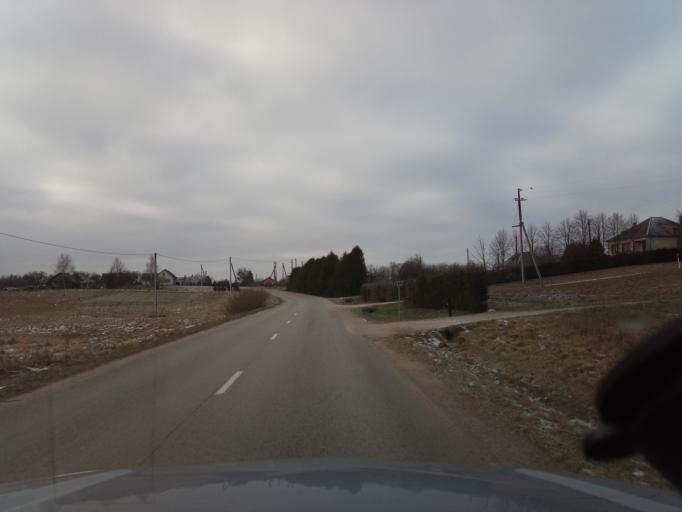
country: LT
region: Alytaus apskritis
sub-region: Alytaus rajonas
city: Daugai
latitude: 54.3541
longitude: 24.3300
